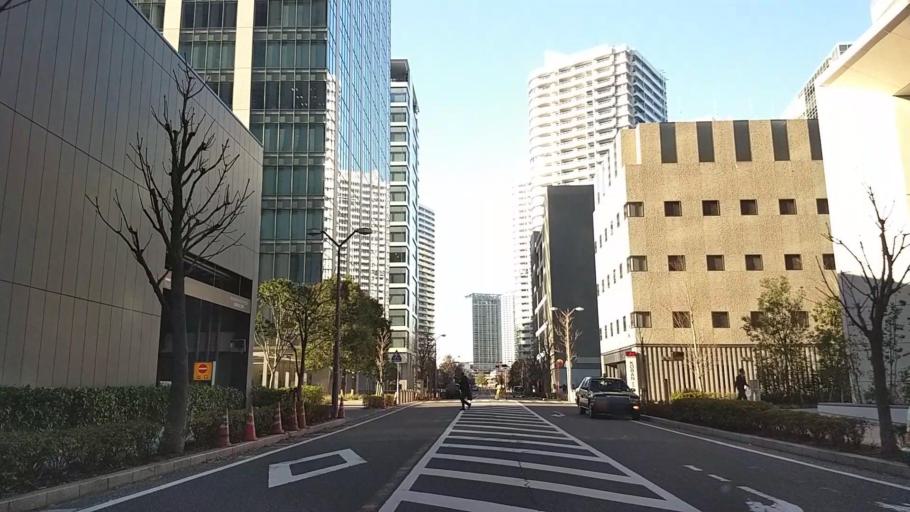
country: JP
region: Kanagawa
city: Yokohama
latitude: 35.4582
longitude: 139.6336
